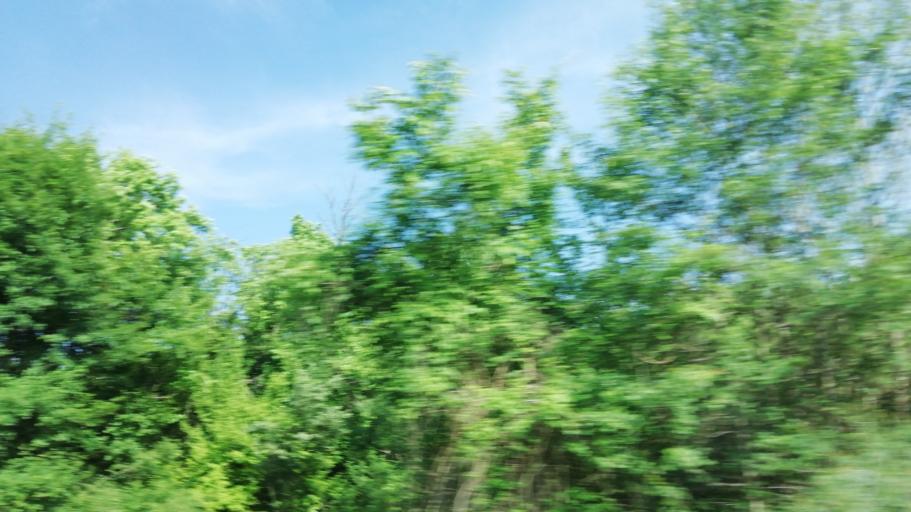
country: TR
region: Karabuk
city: Karabuk
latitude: 41.0835
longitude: 32.5676
